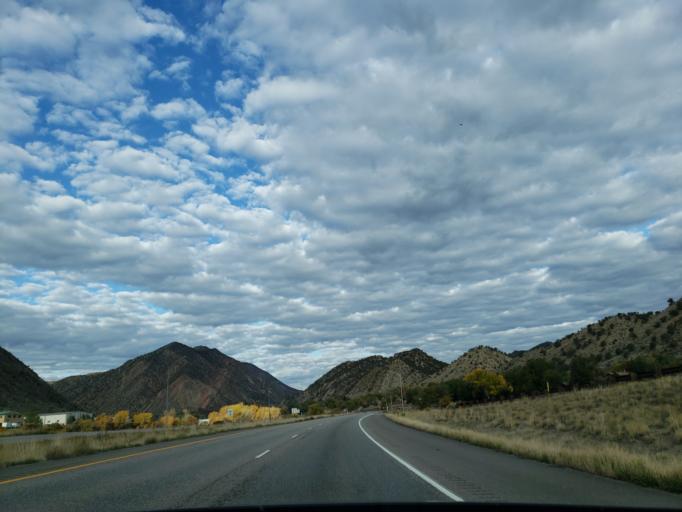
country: US
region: Colorado
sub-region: Garfield County
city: New Castle
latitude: 39.5666
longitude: -107.5189
